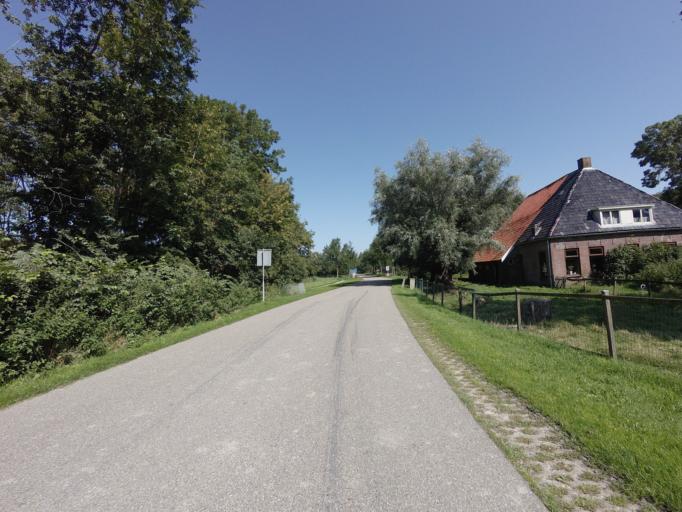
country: NL
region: Friesland
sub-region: Gemeente Dongeradeel
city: Ternaard
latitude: 53.3733
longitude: 5.9981
